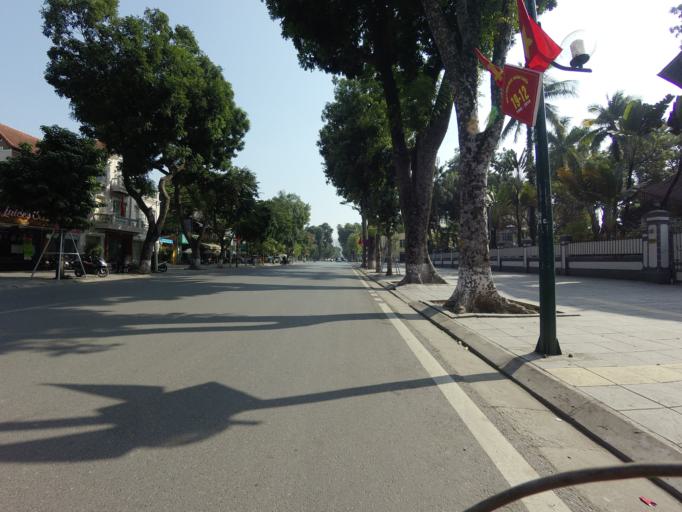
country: VN
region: Ha Noi
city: Hanoi
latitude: 21.0339
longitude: 105.8378
